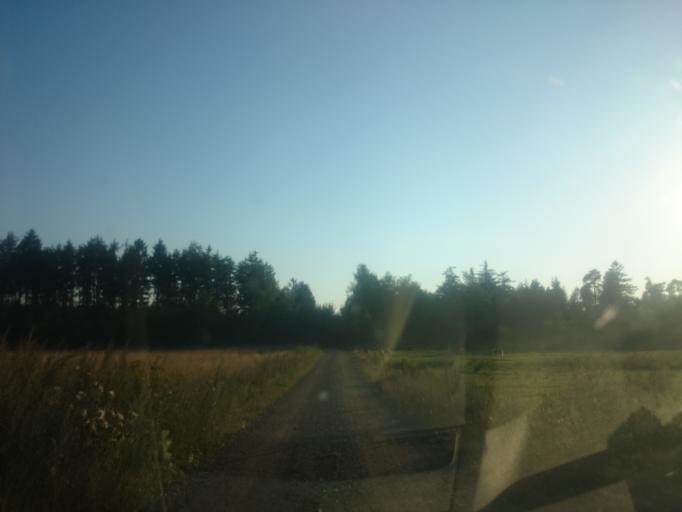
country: DK
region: South Denmark
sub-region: Billund Kommune
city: Billund
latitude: 55.7307
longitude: 9.0414
